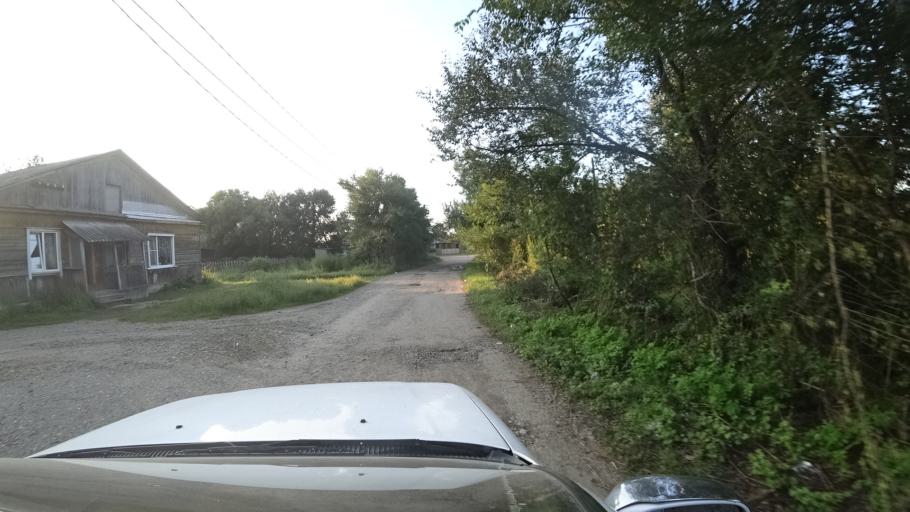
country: RU
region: Primorskiy
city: Dal'nerechensk
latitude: 45.9449
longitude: 133.7555
